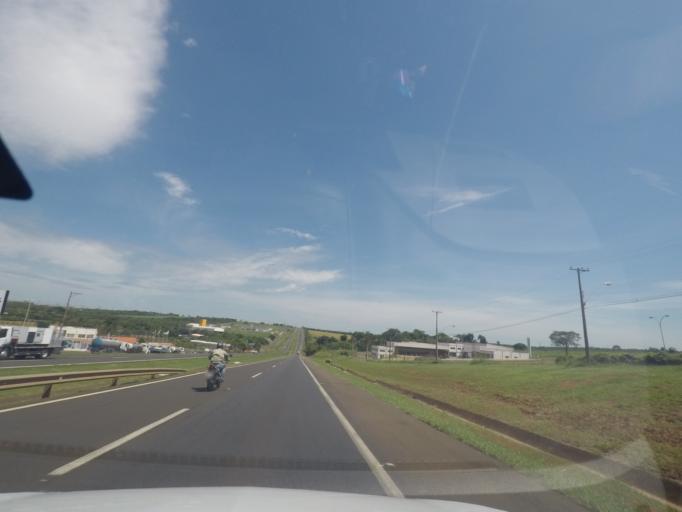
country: BR
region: Sao Paulo
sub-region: Araraquara
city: Araraquara
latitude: -21.7771
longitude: -48.2324
